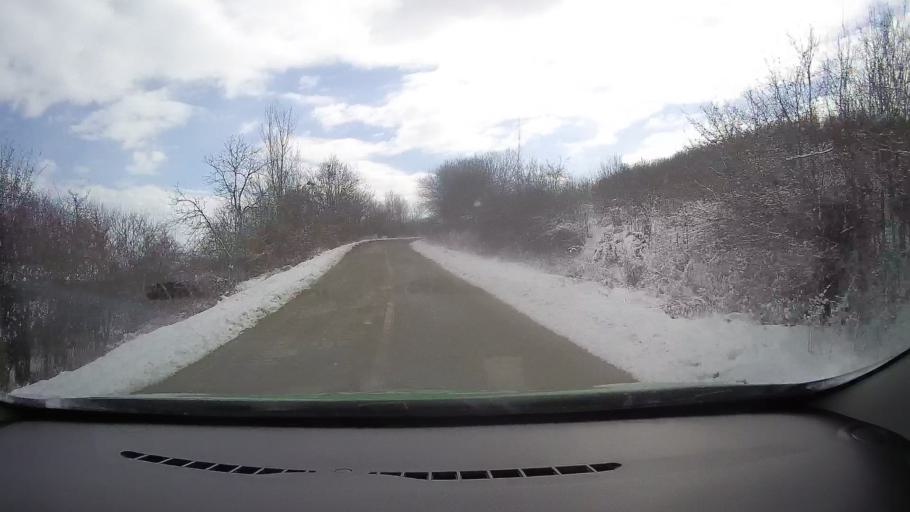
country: RO
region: Sibiu
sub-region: Comuna Altina
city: Altina
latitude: 45.9928
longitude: 24.4333
